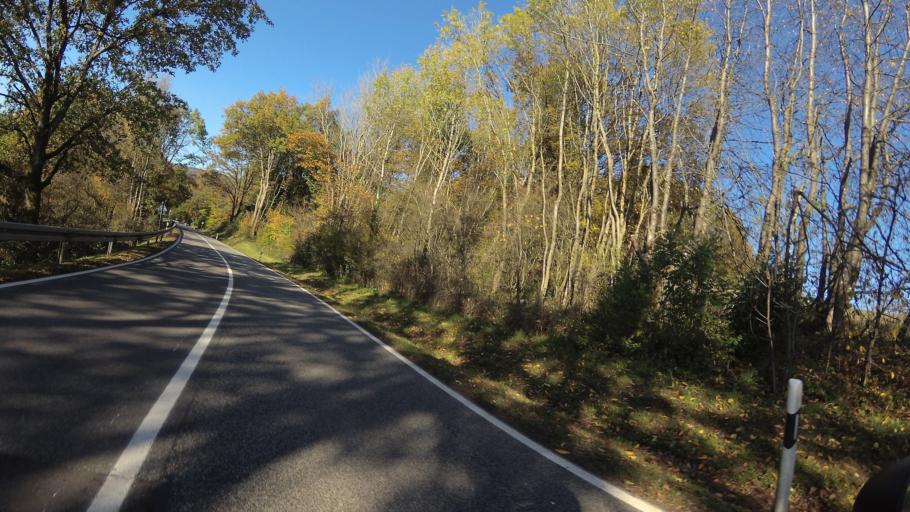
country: DE
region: Saarland
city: Weiskirchen
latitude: 49.5355
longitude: 6.7831
